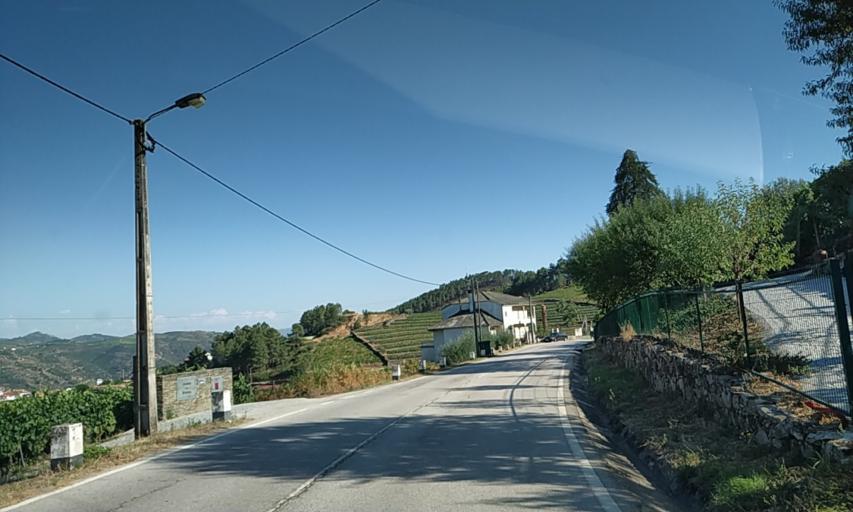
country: PT
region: Viseu
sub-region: Sao Joao da Pesqueira
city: Sao Joao da Pesqueira
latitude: 41.2560
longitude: -7.4404
